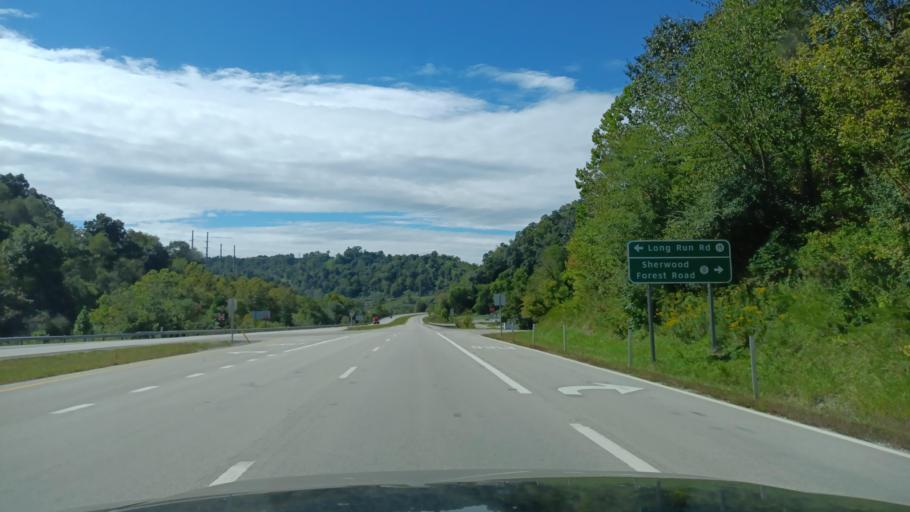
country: US
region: West Virginia
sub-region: Doddridge County
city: West Union
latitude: 39.2802
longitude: -80.6789
